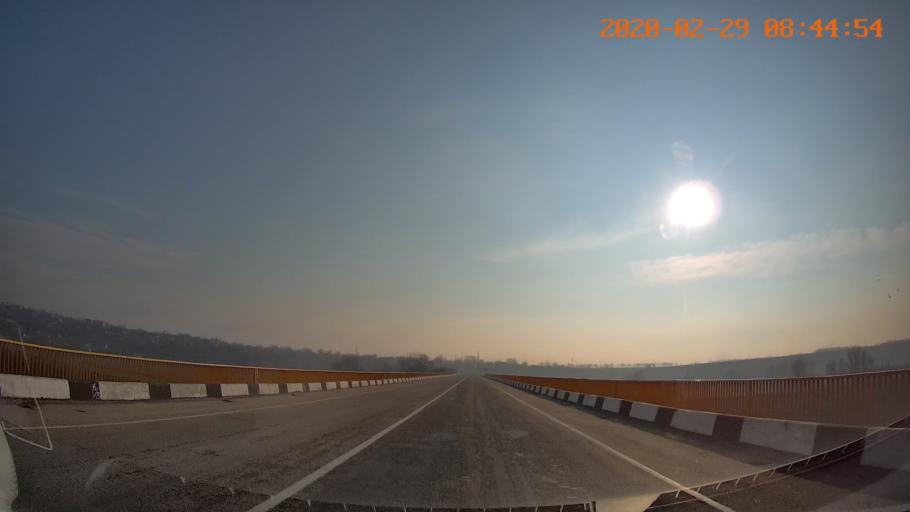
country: MD
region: Anenii Noi
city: Varnita
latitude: 46.9199
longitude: 29.4719
